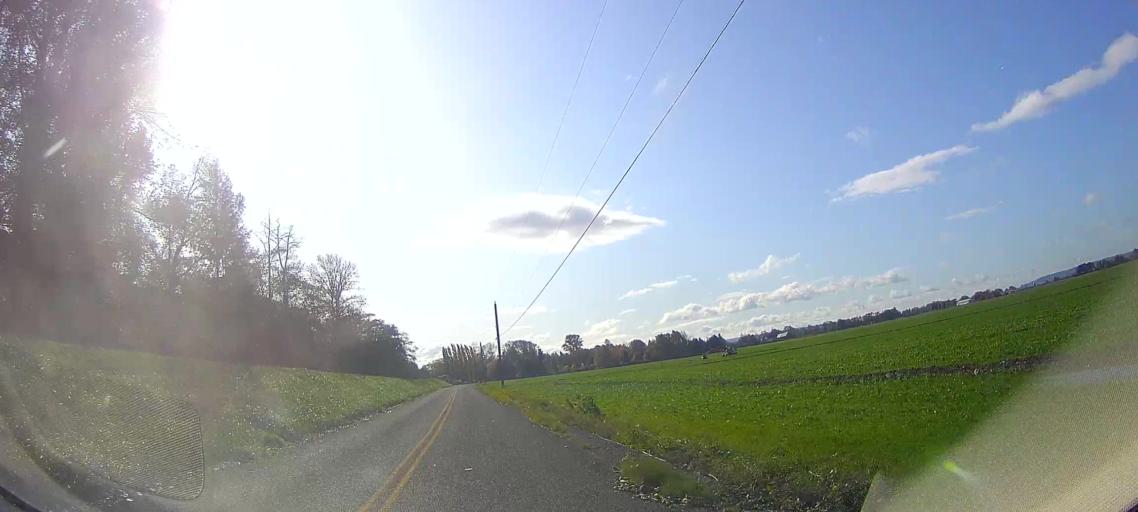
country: US
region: Washington
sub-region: Skagit County
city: Mount Vernon
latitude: 48.3338
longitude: -122.3516
